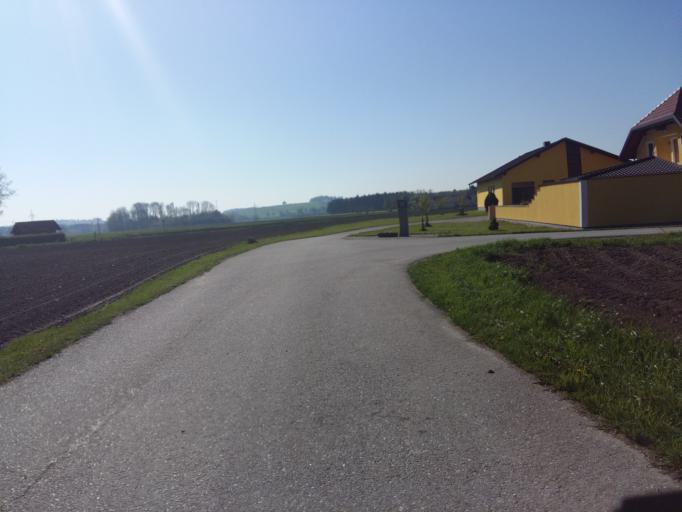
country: AT
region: Upper Austria
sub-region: Politischer Bezirk Scharding
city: Sankt Marienkirchen bei Schaerding
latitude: 48.3944
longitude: 13.4334
